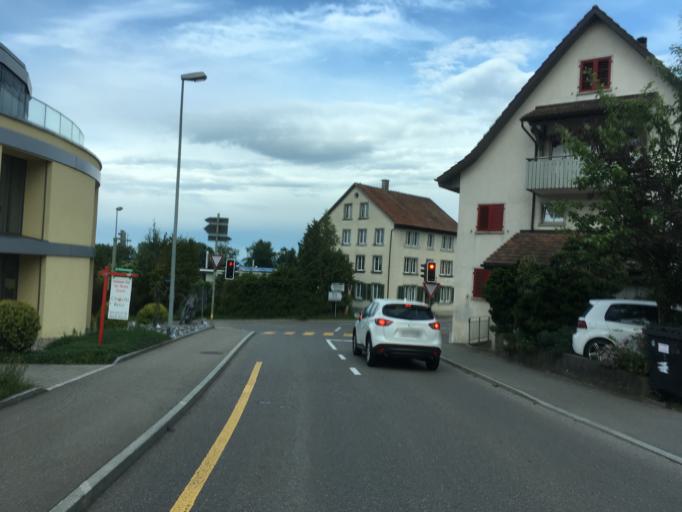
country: CH
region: Zurich
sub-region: Bezirk Uster
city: Binz
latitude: 47.3560
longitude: 8.6297
